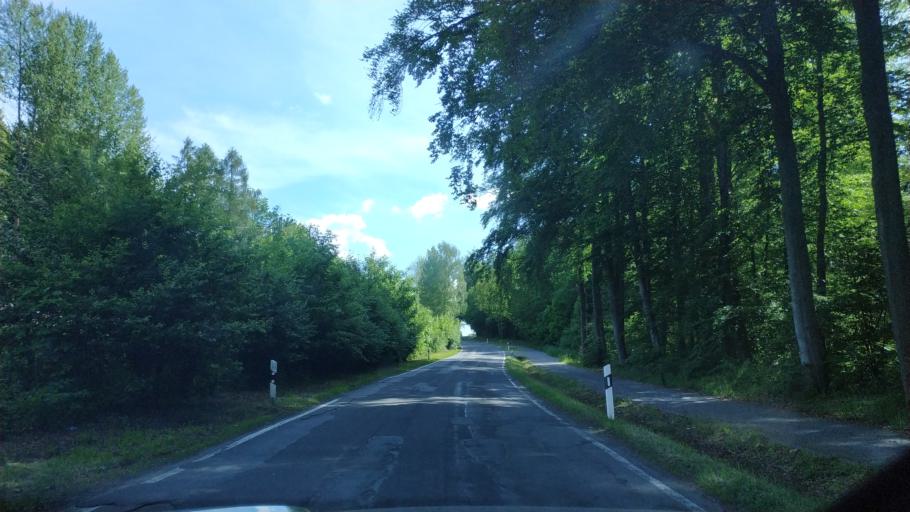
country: DE
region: Saxony
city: Plauen
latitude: 50.5308
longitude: 12.1345
